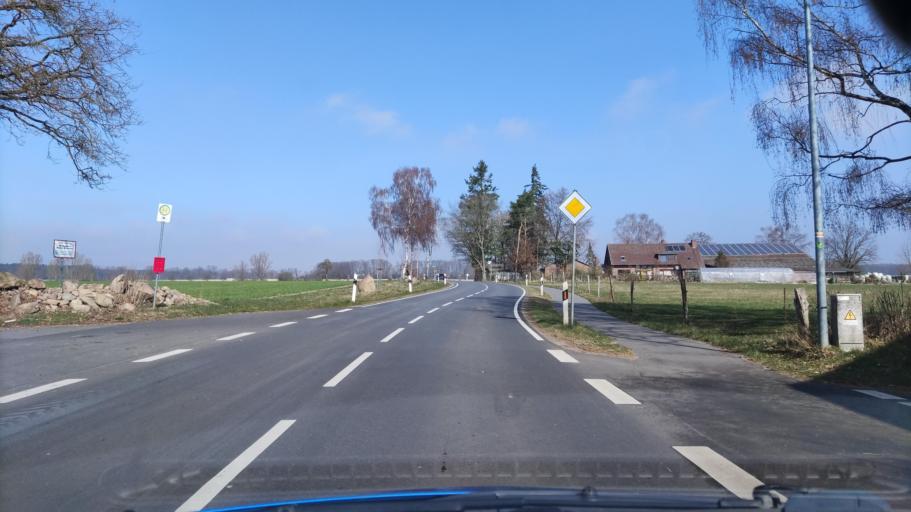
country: DE
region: Lower Saxony
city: Waddeweitz
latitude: 52.9673
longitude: 10.9715
